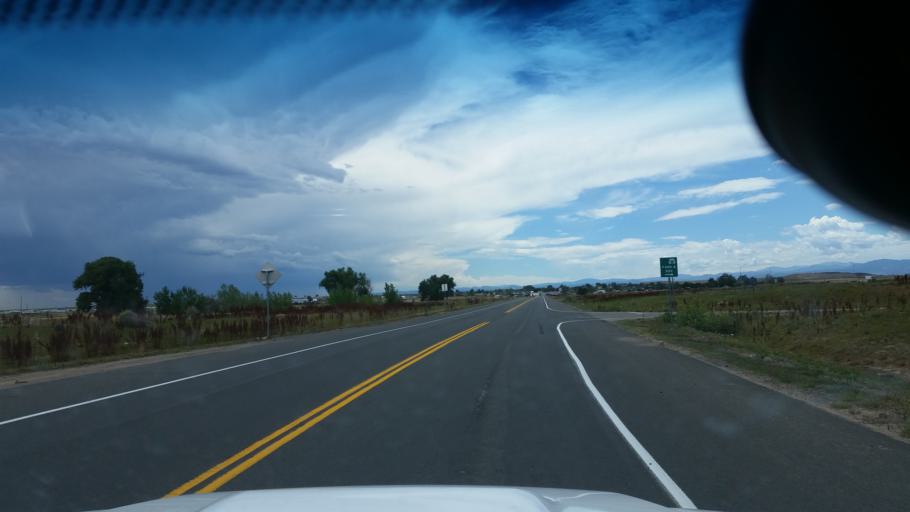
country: US
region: Colorado
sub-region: Weld County
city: Dacono
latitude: 40.0428
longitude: -104.9767
